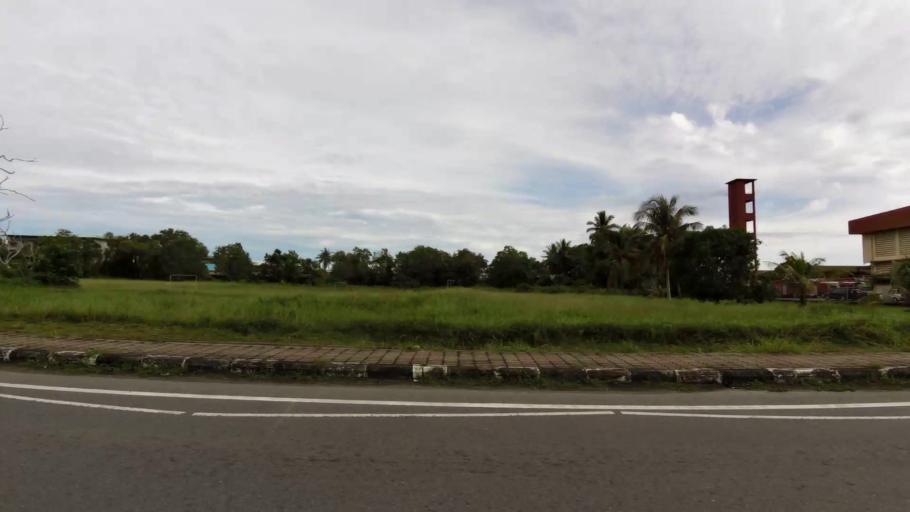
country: BN
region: Belait
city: Seria
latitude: 4.6141
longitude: 114.3368
